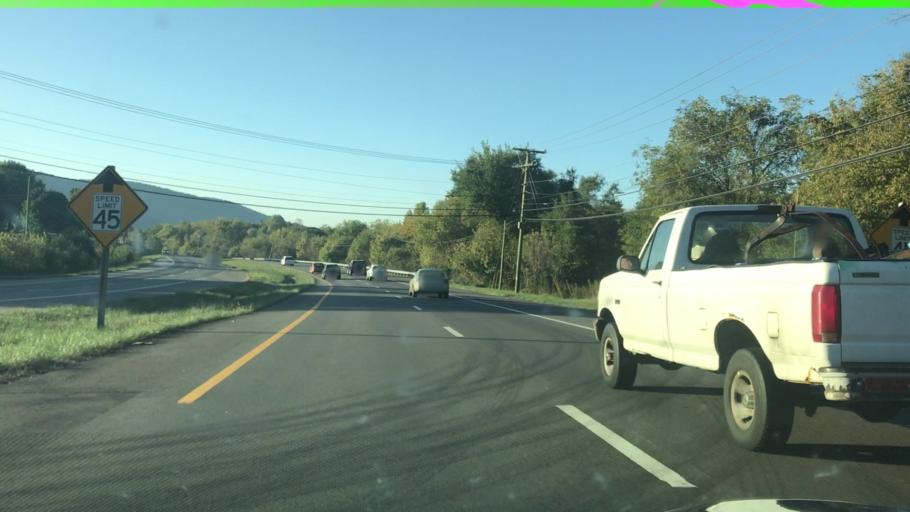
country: US
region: Virginia
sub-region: Botetourt County
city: Laymantown
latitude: 37.3379
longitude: -79.8758
